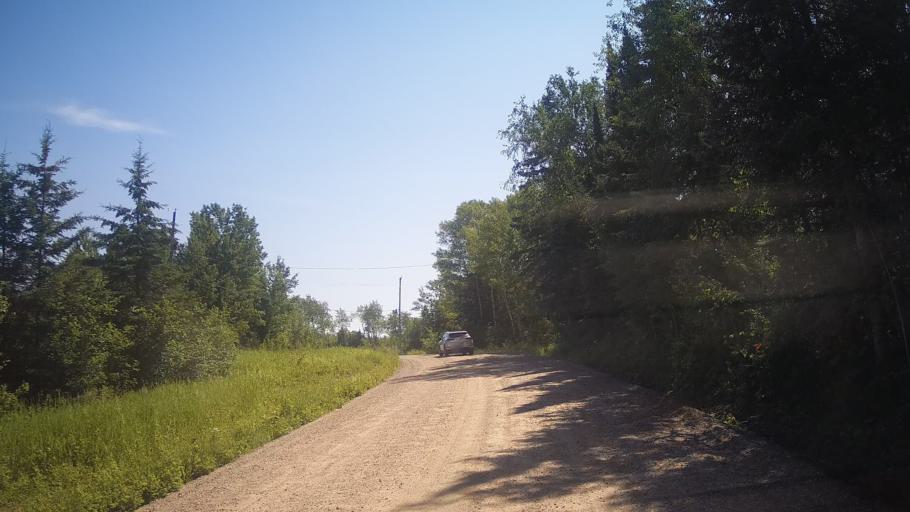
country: CA
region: Ontario
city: Dryden
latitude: 49.8153
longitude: -93.3252
